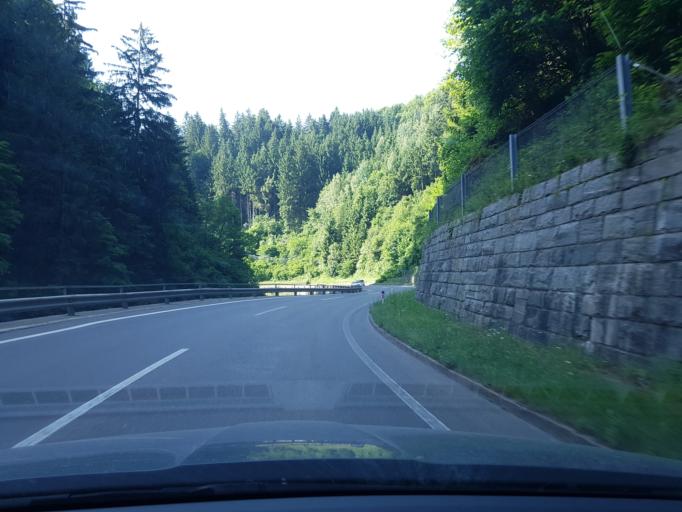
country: AT
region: Carinthia
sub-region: Politischer Bezirk Spittal an der Drau
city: Spittal an der Drau
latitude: 46.8116
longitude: 13.4917
